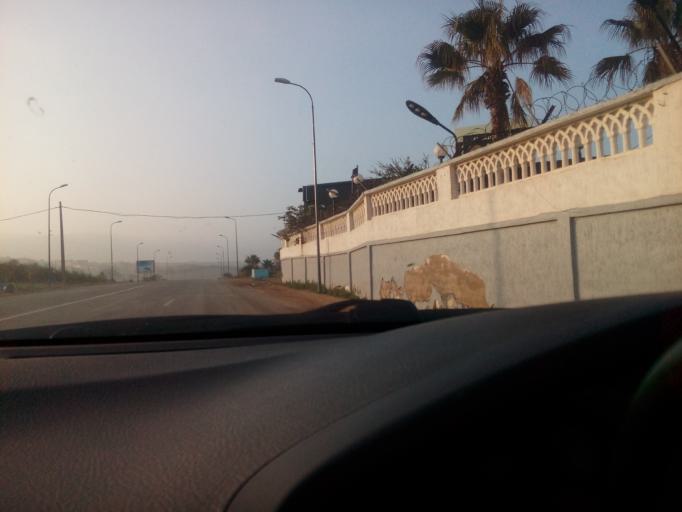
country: DZ
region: Oran
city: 'Ain el Turk
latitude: 35.7324
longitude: -0.8415
